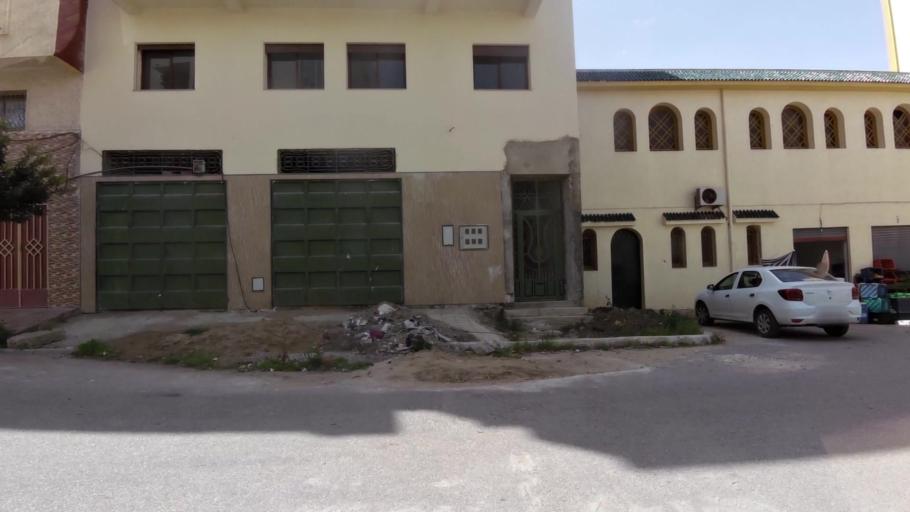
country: MA
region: Tanger-Tetouan
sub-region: Tanger-Assilah
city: Tangier
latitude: 35.7568
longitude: -5.8389
